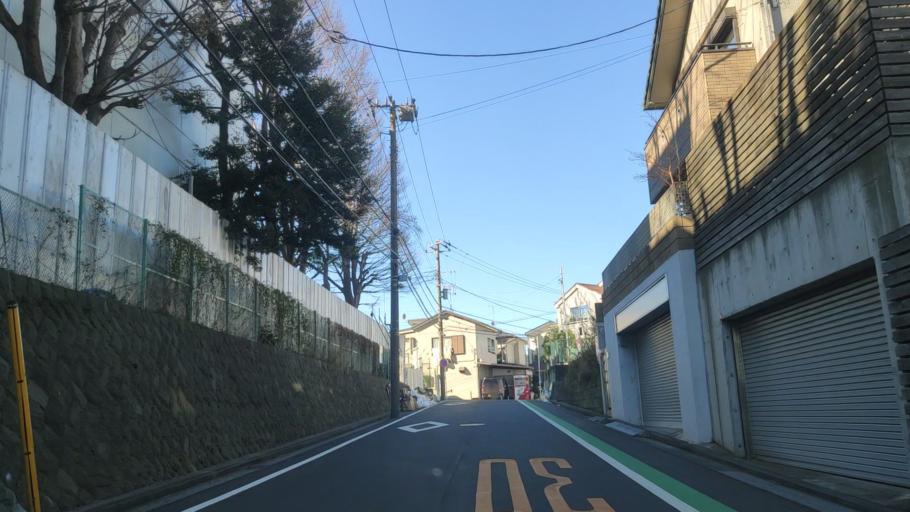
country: JP
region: Kanagawa
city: Yokohama
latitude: 35.4252
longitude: 139.6526
